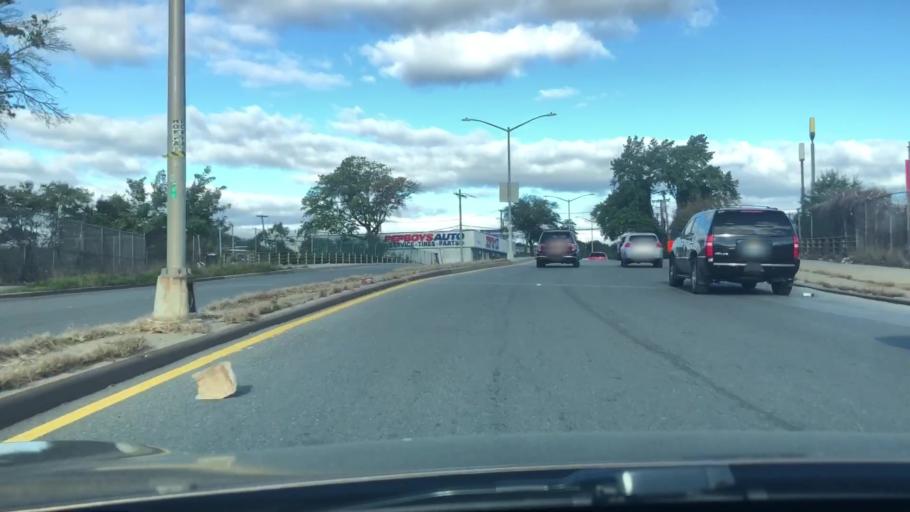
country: US
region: New York
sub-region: Bronx
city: Eastchester
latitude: 40.8835
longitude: -73.8252
